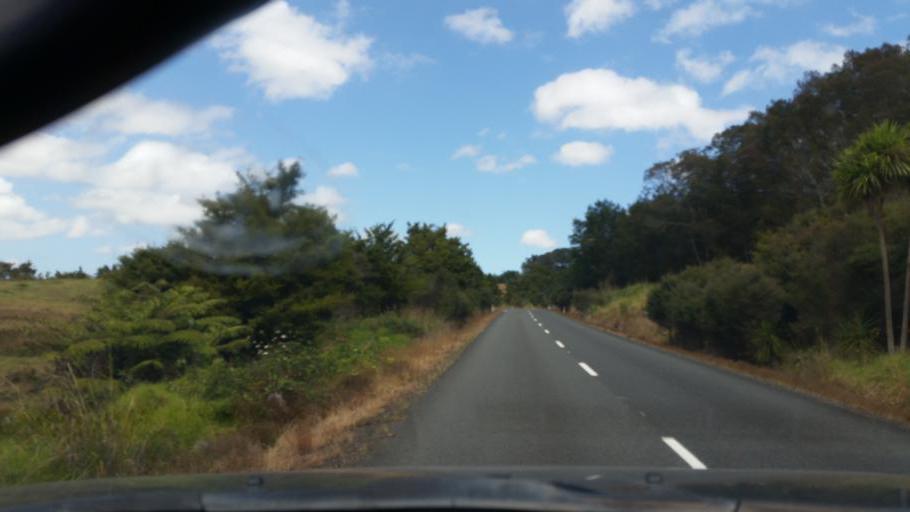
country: NZ
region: Northland
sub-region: Kaipara District
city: Dargaville
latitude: -35.8687
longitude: 173.8429
